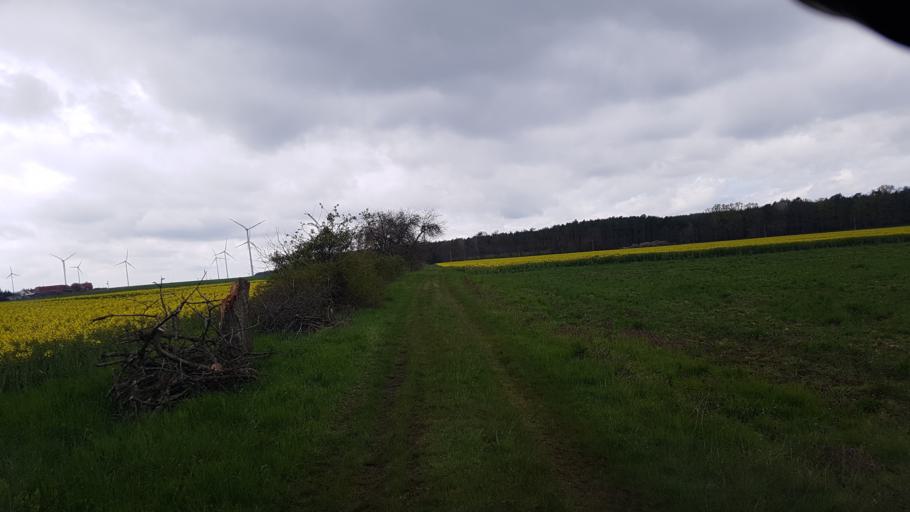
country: DE
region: Brandenburg
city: Schonborn
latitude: 51.6734
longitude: 13.4837
